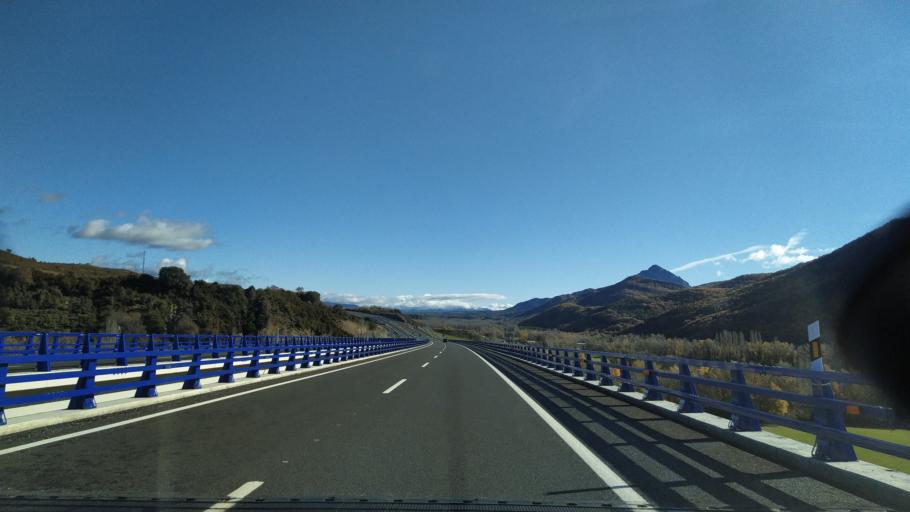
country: ES
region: Aragon
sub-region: Provincia de Huesca
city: Santa Cruz de la Seros
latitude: 42.5618
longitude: -0.6693
